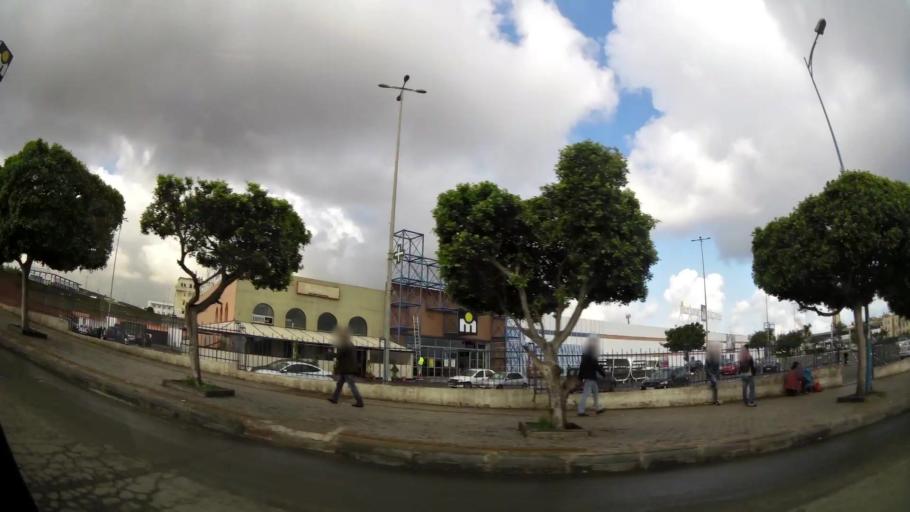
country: MA
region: Grand Casablanca
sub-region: Mediouna
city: Tit Mellil
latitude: 33.5956
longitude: -7.5302
